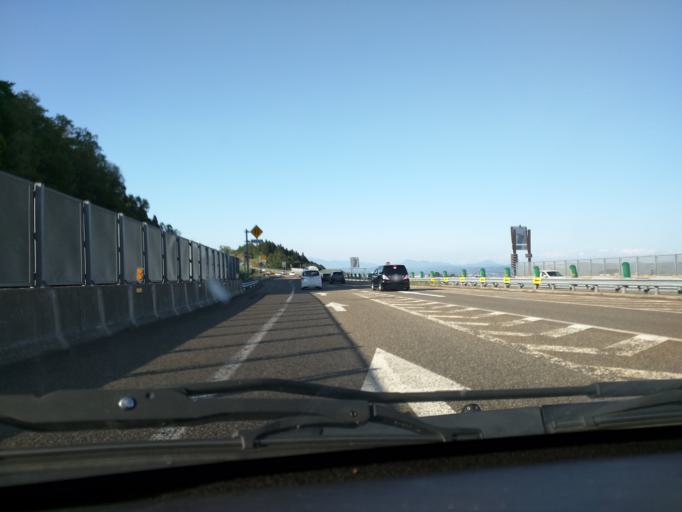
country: JP
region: Niigata
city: Arai
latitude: 37.0297
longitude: 138.2273
